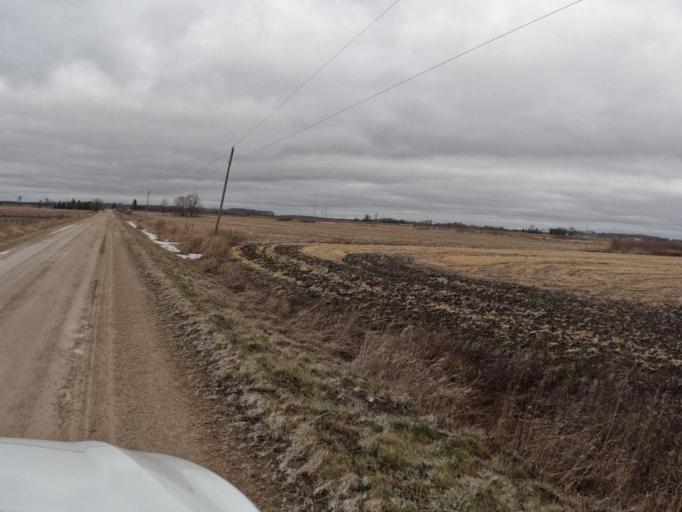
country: CA
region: Ontario
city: Shelburne
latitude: 44.0332
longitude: -80.3718
